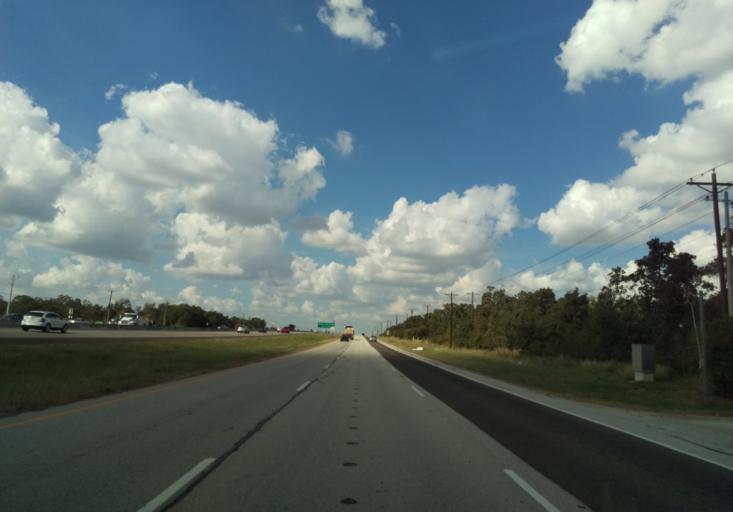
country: US
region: Texas
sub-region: Brazos County
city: College Station
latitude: 30.5647
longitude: -96.2644
